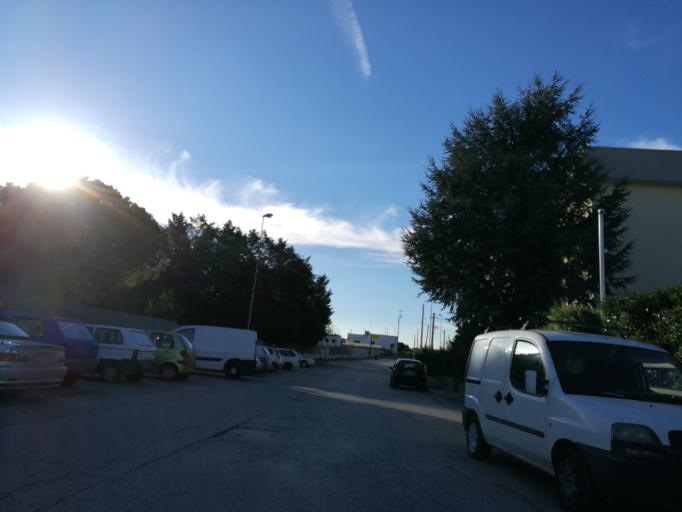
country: IT
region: Apulia
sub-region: Provincia di Bari
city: Adelfia
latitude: 41.0027
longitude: 16.8635
